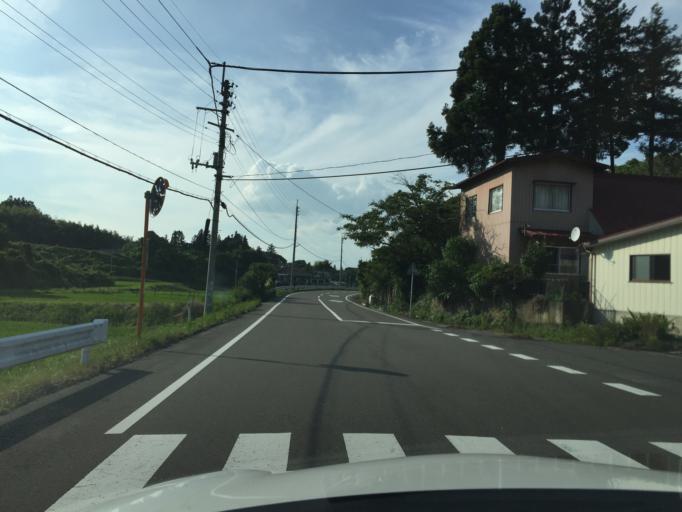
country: JP
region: Fukushima
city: Miharu
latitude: 37.3715
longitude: 140.5140
